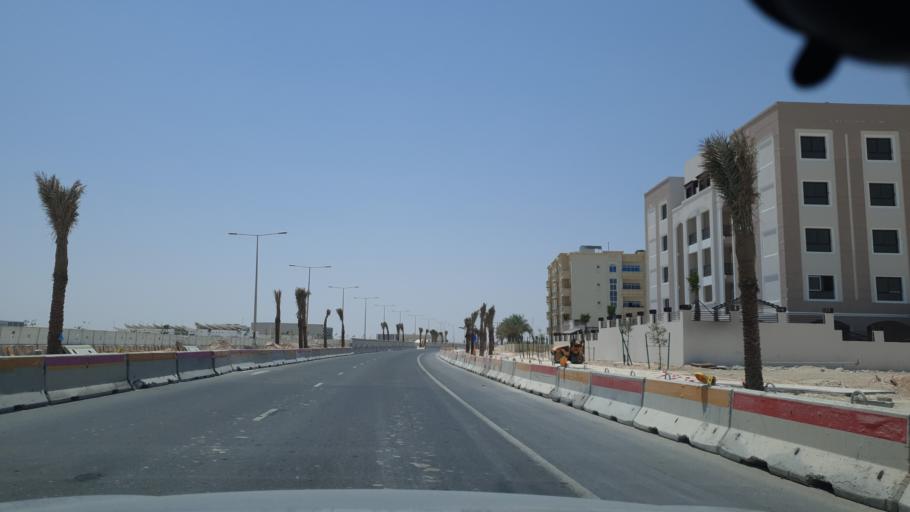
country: QA
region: Baladiyat Umm Salal
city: Umm Salal Muhammad
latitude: 25.4075
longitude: 51.5104
